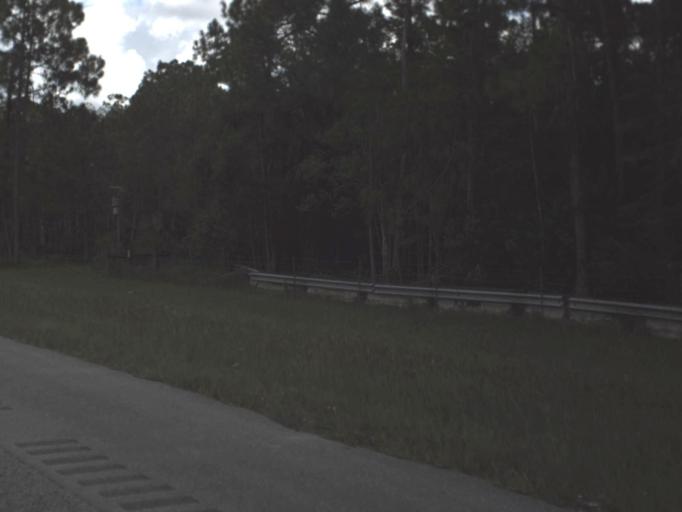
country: US
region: Florida
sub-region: Collier County
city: Golden Gate
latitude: 26.1548
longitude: -81.6530
